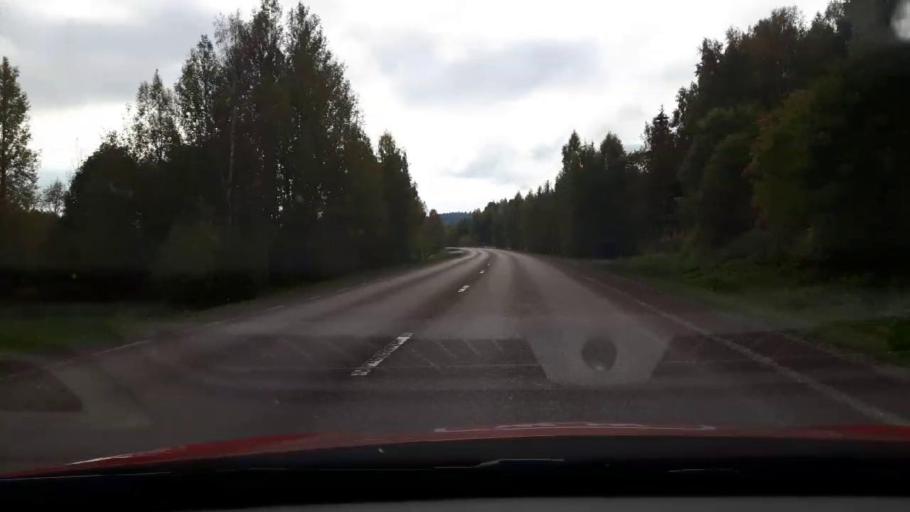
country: SE
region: Gaevleborg
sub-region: Ljusdals Kommun
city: Jaervsoe
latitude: 61.6106
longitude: 16.2952
